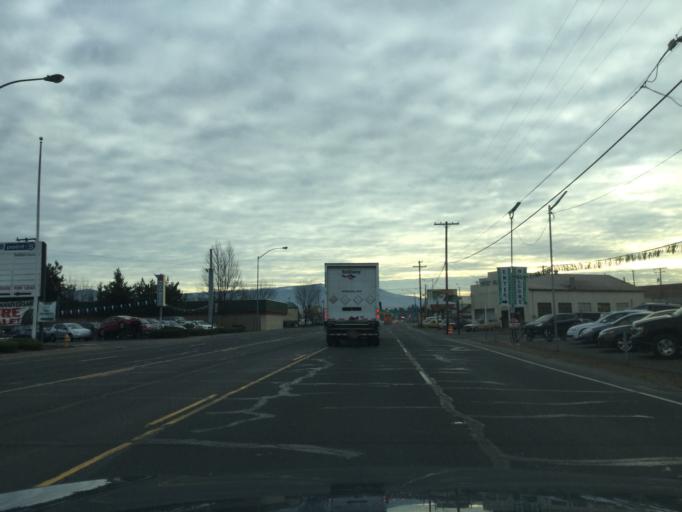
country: US
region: Oregon
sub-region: Jackson County
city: Medford
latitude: 42.3478
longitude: -122.8876
